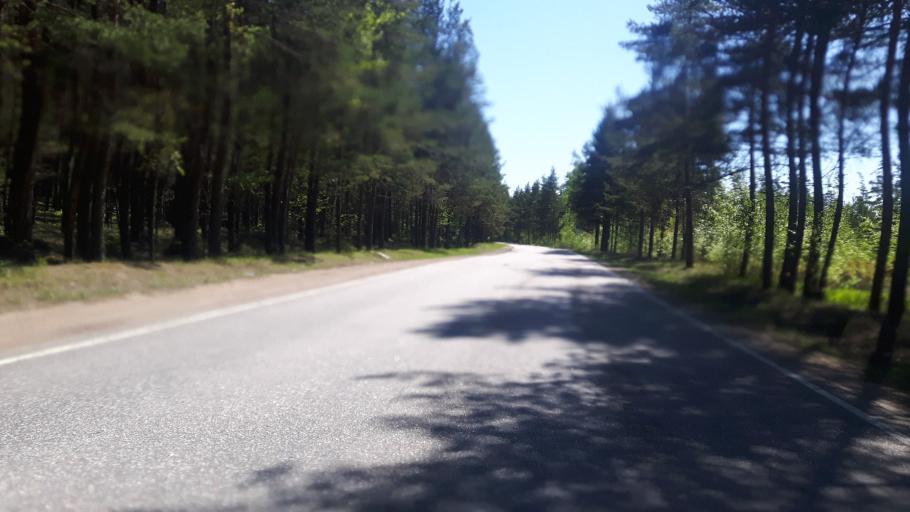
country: RU
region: Leningrad
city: Glebychevo
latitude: 60.3493
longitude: 28.8179
